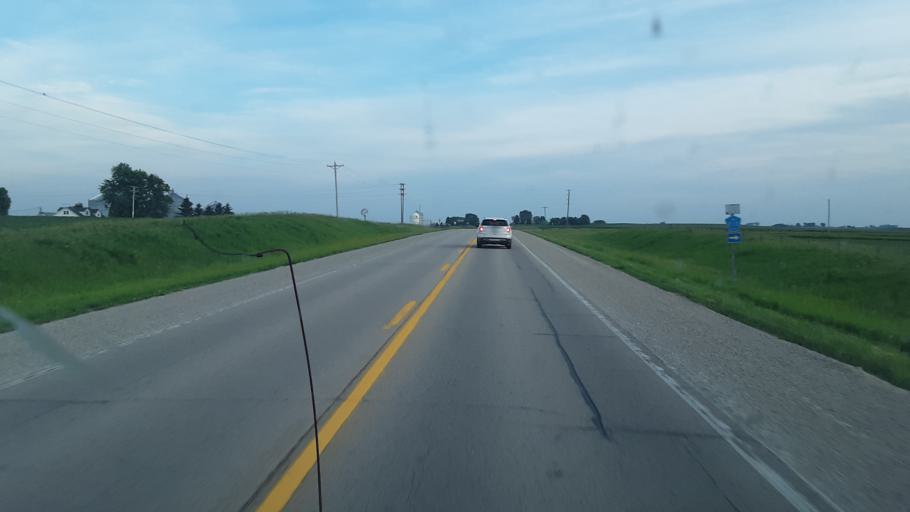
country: US
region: Iowa
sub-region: Benton County
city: Belle Plaine
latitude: 41.7998
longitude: -92.2788
